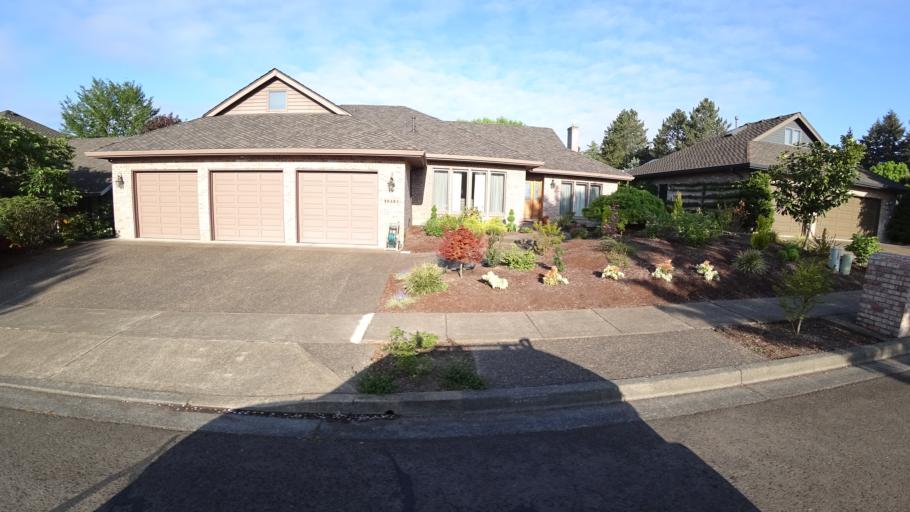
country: US
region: Oregon
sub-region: Washington County
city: Beaverton
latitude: 45.4454
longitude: -122.8193
